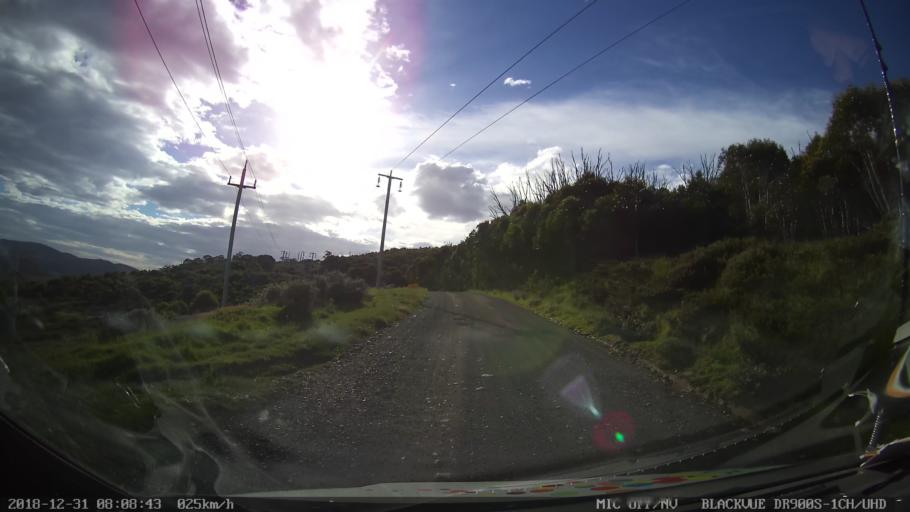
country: AU
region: New South Wales
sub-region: Snowy River
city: Jindabyne
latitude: -36.3808
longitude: 148.4142
